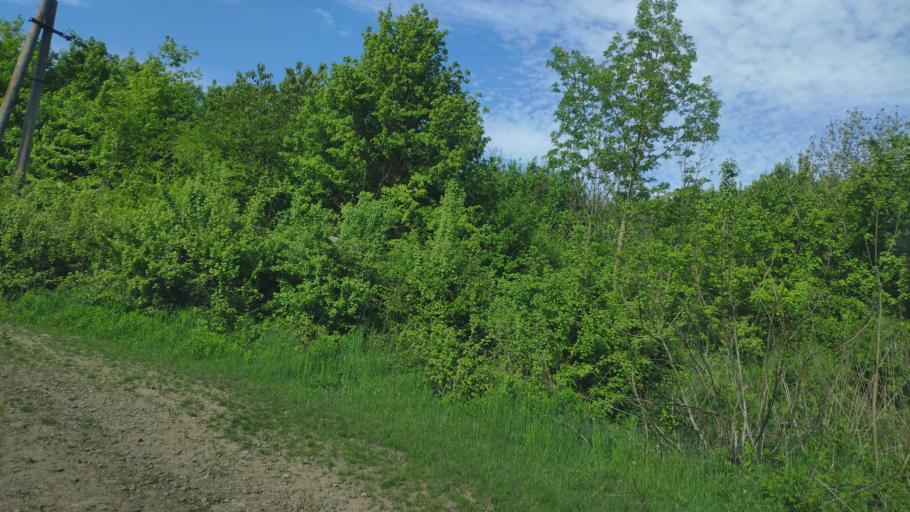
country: SK
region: Kosicky
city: Secovce
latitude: 48.7100
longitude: 21.6143
